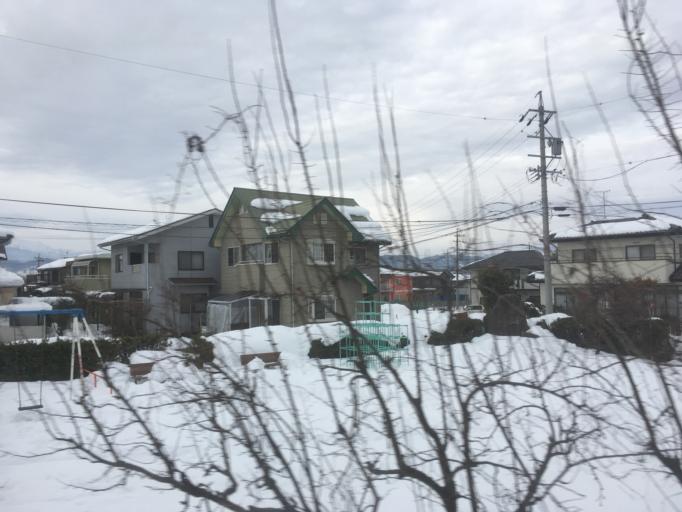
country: JP
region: Nagano
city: Suzaka
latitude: 36.7025
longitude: 138.3190
